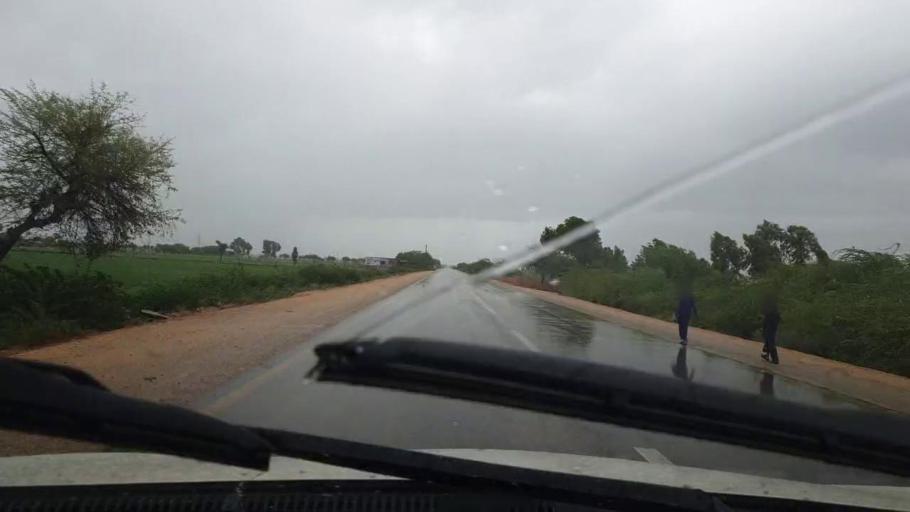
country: PK
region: Sindh
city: Kario
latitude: 24.6534
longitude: 68.5760
